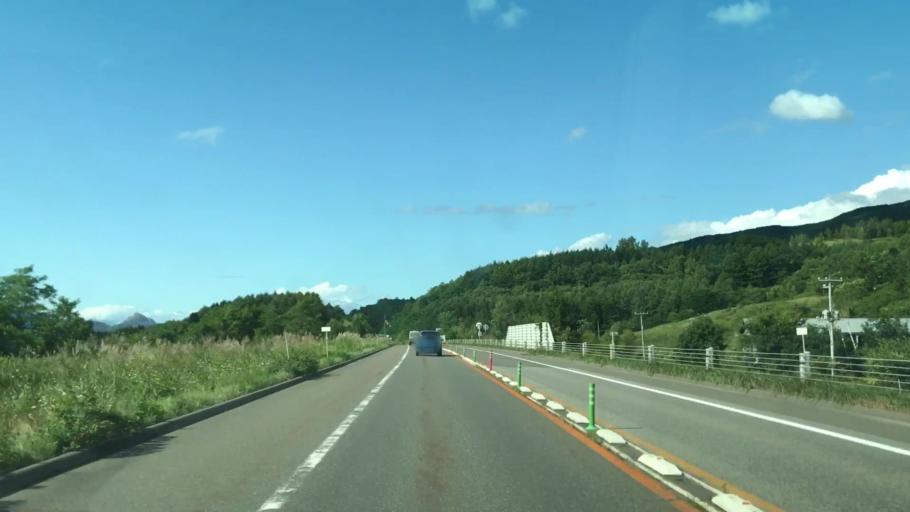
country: JP
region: Hokkaido
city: Date
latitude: 42.4519
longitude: 140.9132
